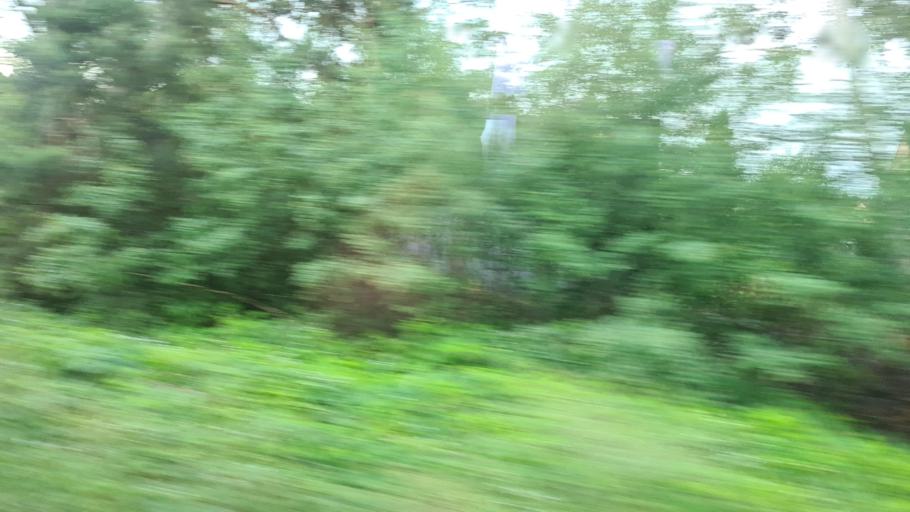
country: DE
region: Brandenburg
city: Schonborn
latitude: 51.6022
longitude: 13.4652
